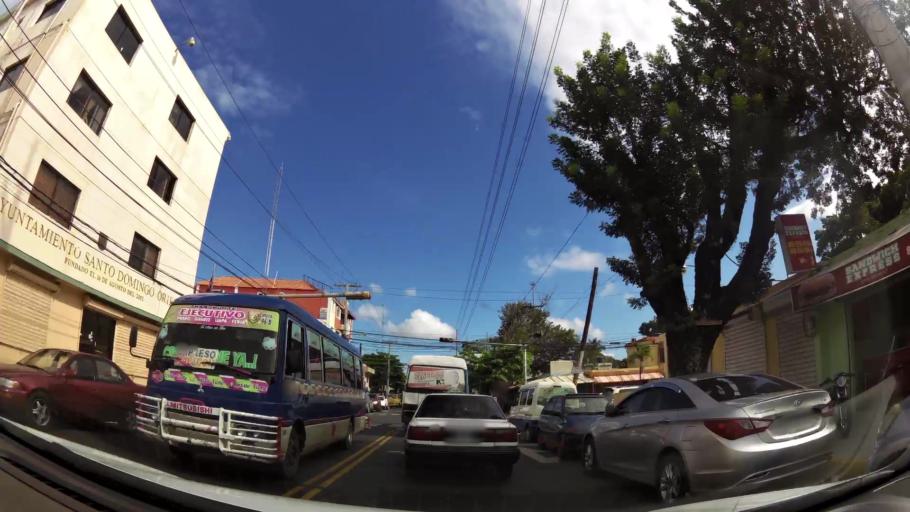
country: DO
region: Santo Domingo
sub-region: Santo Domingo
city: Santo Domingo Este
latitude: 18.4900
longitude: -69.8653
